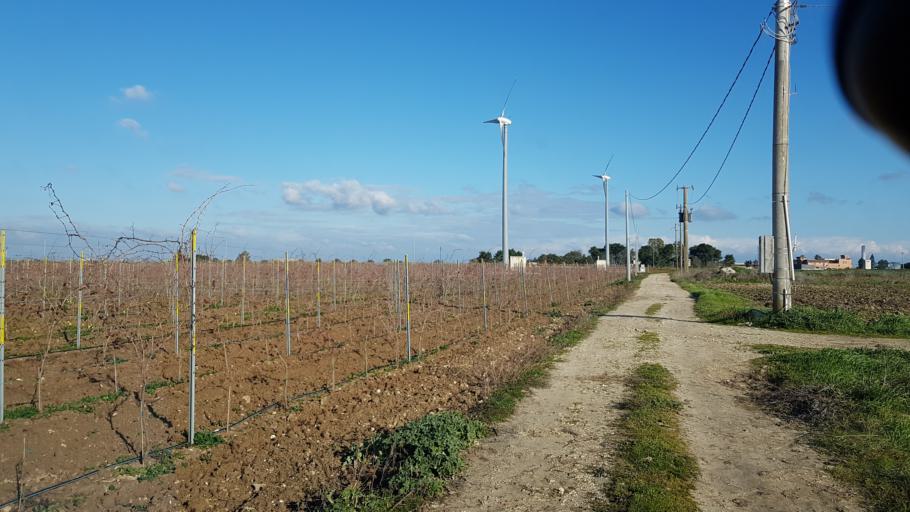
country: IT
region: Apulia
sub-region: Provincia di Brindisi
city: Tuturano
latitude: 40.5700
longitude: 17.9616
